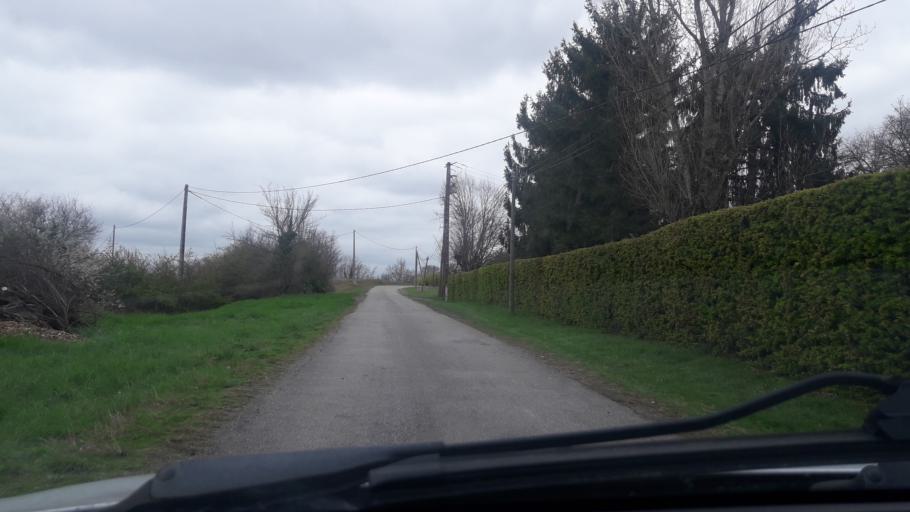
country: FR
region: Midi-Pyrenees
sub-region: Departement de l'Ariege
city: Lezat-sur-Leze
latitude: 43.1784
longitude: 1.3273
